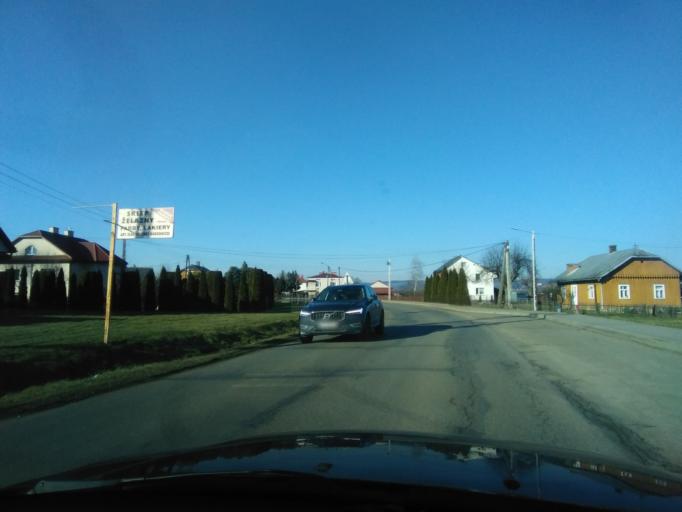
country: PL
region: Subcarpathian Voivodeship
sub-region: Powiat brzozowski
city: Haczow
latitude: 49.6734
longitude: 21.8872
